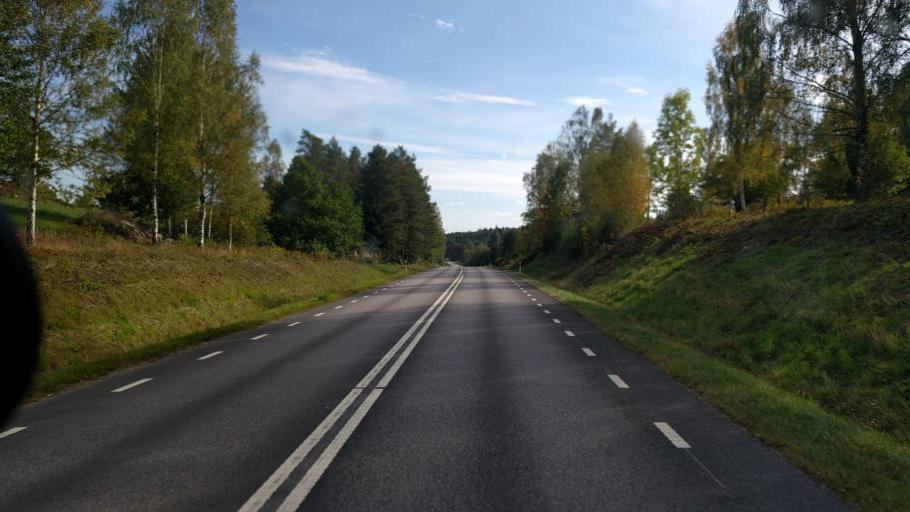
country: SE
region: OEstergoetland
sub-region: Kinda Kommun
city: Kisa
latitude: 57.9189
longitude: 15.6805
